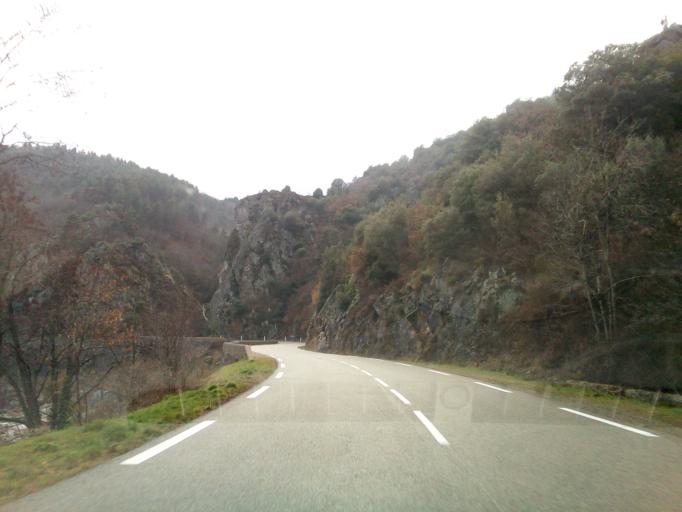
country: FR
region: Rhone-Alpes
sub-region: Departement de l'Ardeche
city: Saint-Sauveur-de-Montagut
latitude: 44.8658
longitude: 4.5526
